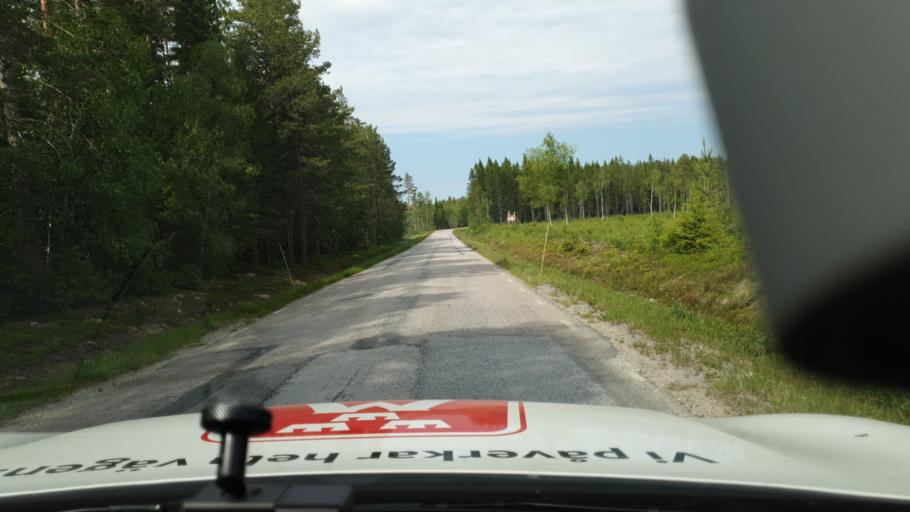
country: SE
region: Vaesterbotten
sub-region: Nordmalings Kommun
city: Nordmaling
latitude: 63.5258
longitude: 19.7105
